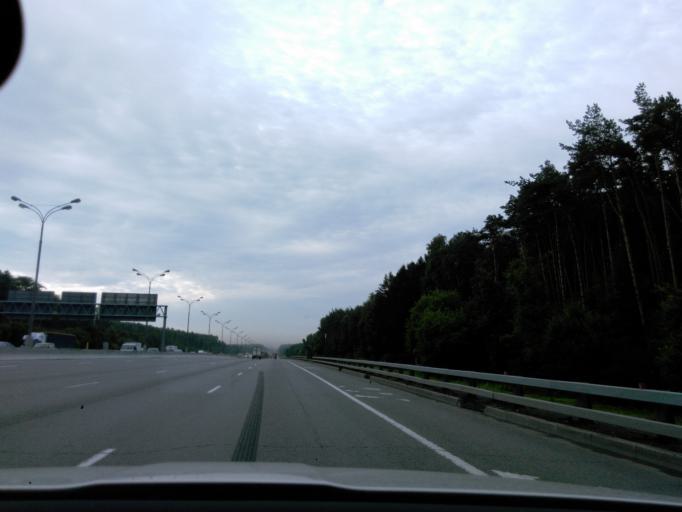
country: RU
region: Moscow
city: Babushkin
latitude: 55.8774
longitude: 37.7355
